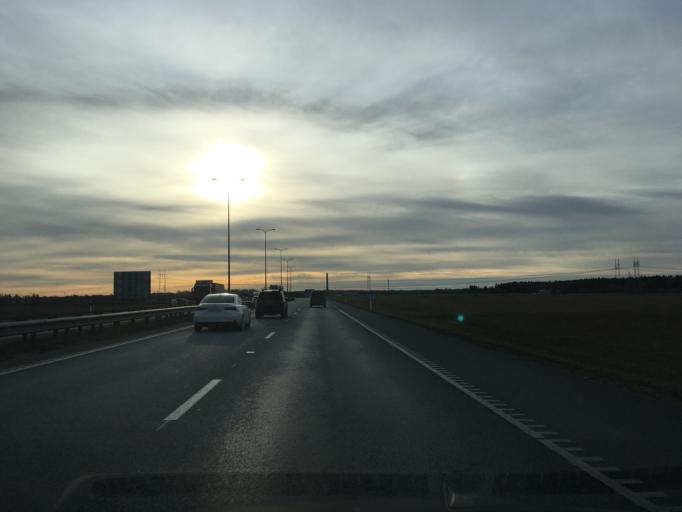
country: EE
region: Ida-Virumaa
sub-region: Kohtla-Jaerve linn
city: Kohtla-Jarve
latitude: 59.3945
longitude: 27.3355
